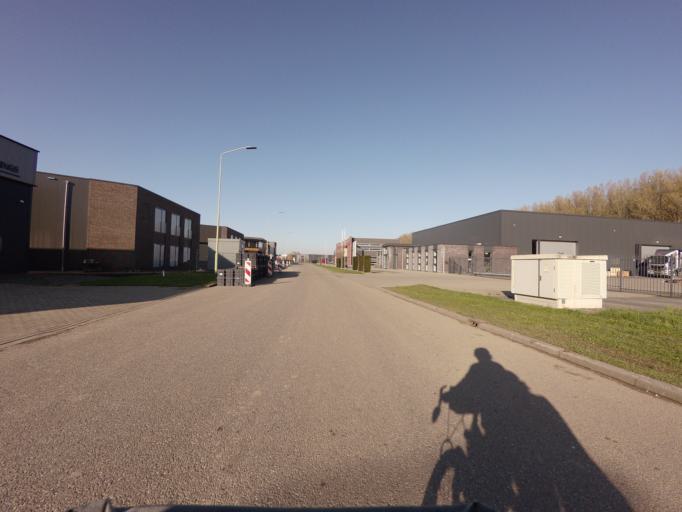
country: NL
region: North Brabant
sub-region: Gemeente Werkendam
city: Werkendam
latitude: 51.7997
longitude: 4.8973
